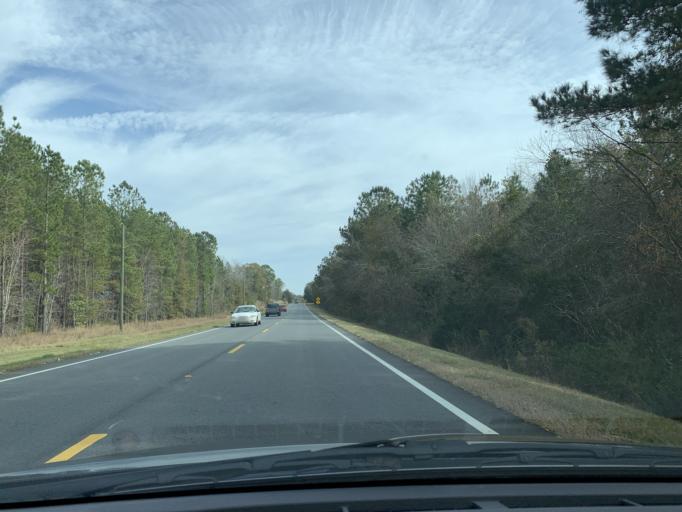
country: US
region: Georgia
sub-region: Wilcox County
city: Rochelle
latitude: 31.9588
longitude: -83.6051
